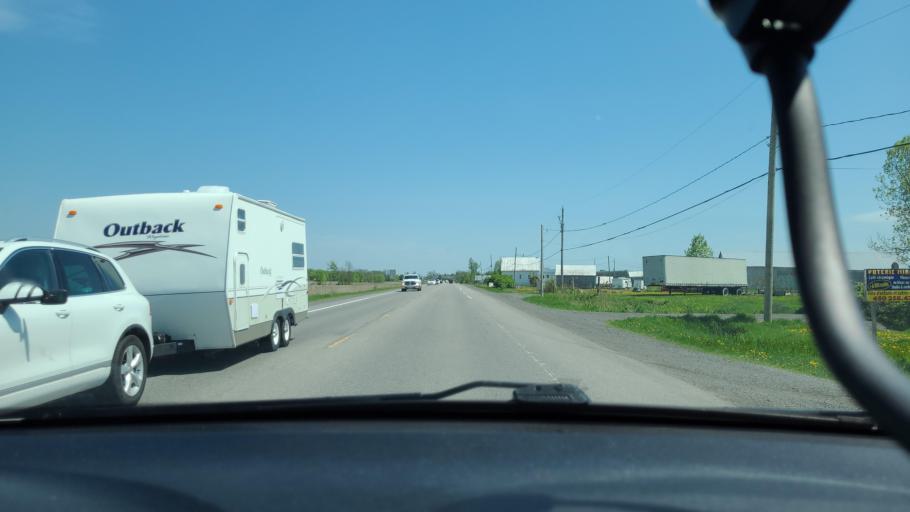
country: CA
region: Quebec
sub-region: Laurentides
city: Mirabel
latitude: 45.6258
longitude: -74.1150
